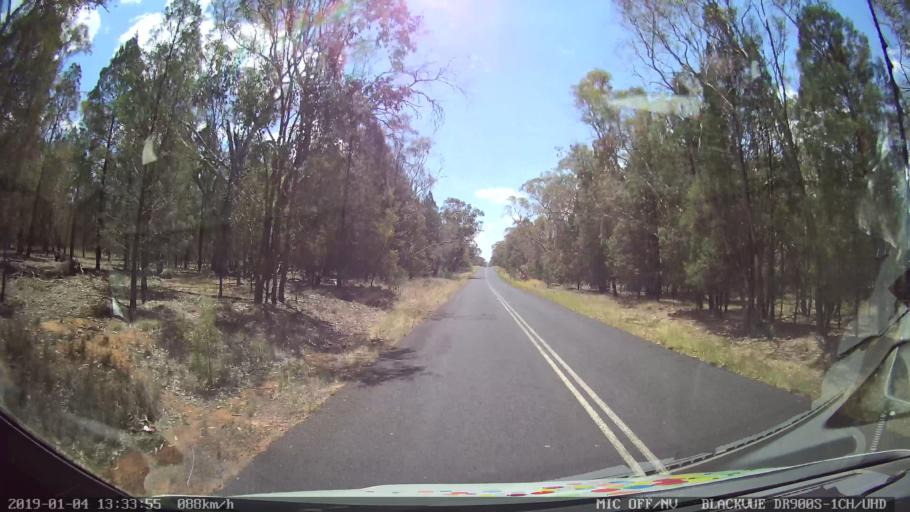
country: AU
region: New South Wales
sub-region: Dubbo Municipality
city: Dubbo
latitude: -32.5926
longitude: 148.5376
